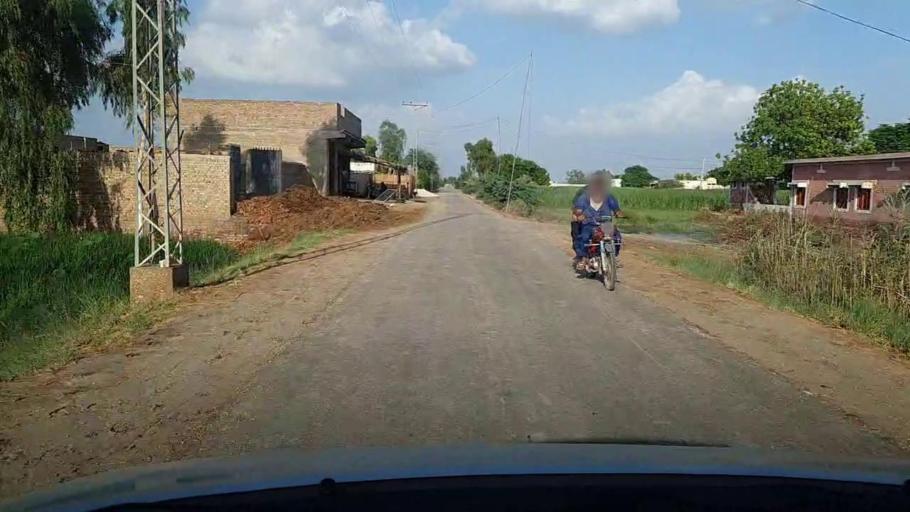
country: PK
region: Sindh
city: Hingorja
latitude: 27.0882
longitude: 68.4061
